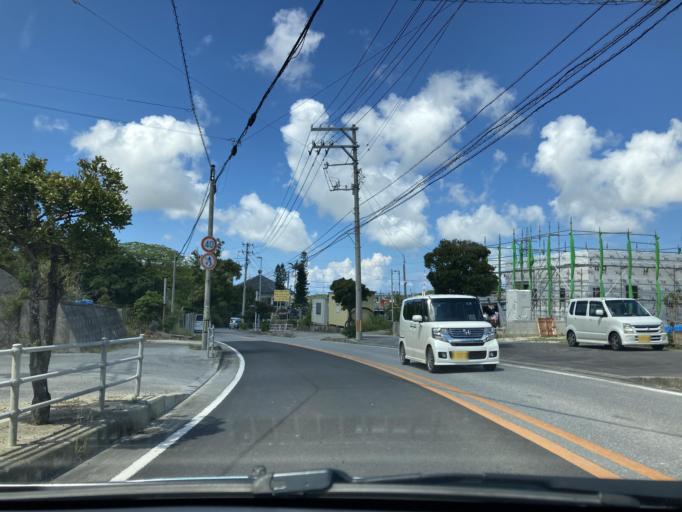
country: JP
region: Okinawa
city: Tomigusuku
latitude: 26.1656
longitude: 127.7222
